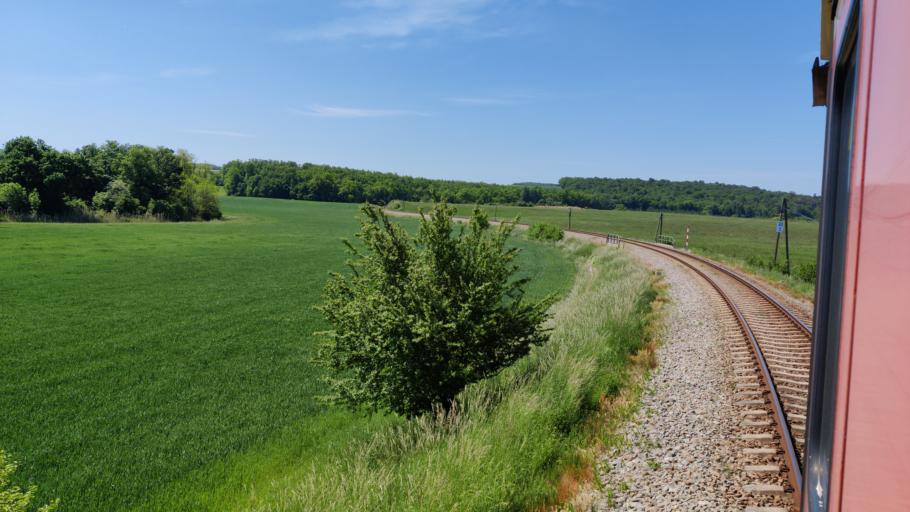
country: AT
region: Lower Austria
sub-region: Politischer Bezirk Horn
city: Horn
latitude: 48.6381
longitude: 15.6802
